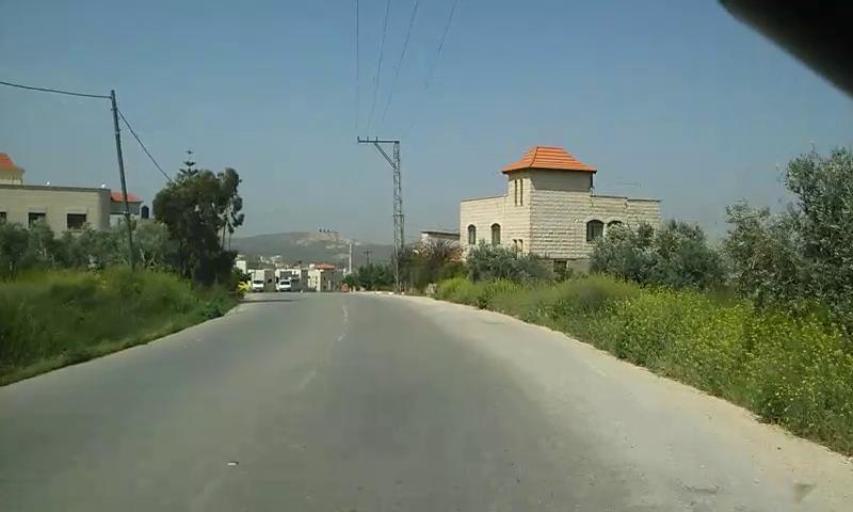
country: PS
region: West Bank
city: Az Zababidah
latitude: 32.3811
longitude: 35.3298
